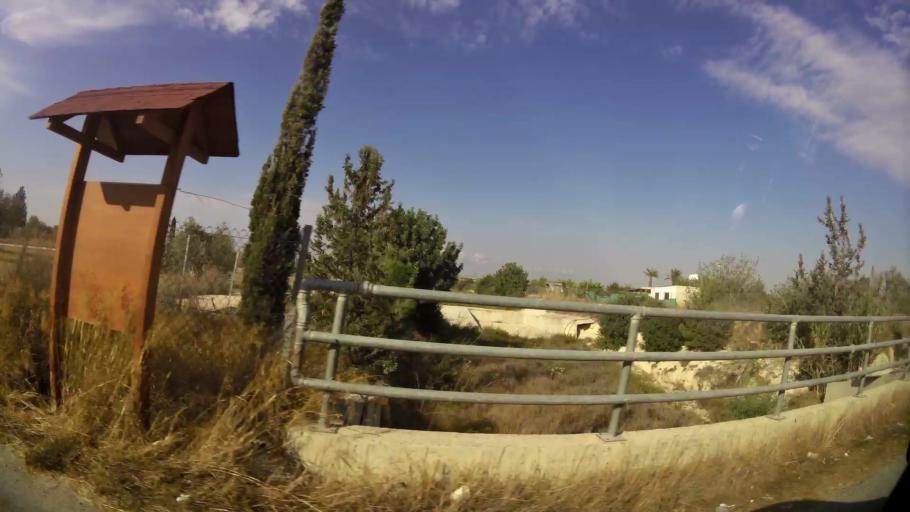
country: CY
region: Larnaka
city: Aradippou
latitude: 34.9568
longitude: 33.6083
